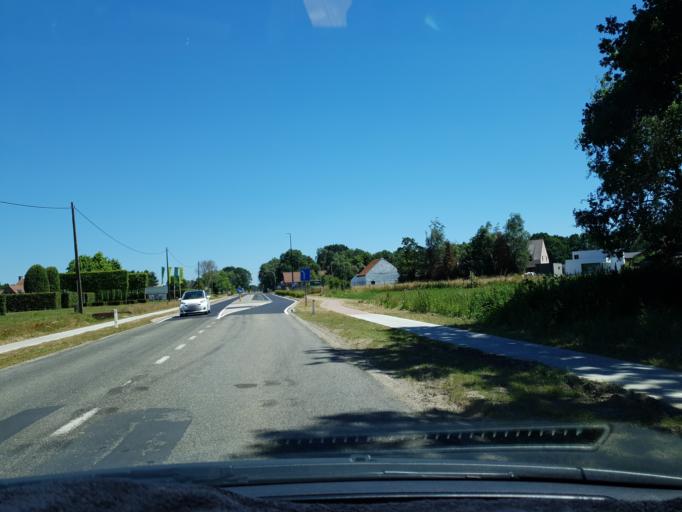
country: BE
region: Flanders
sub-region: Provincie Antwerpen
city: Olen
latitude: 51.1601
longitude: 4.8815
